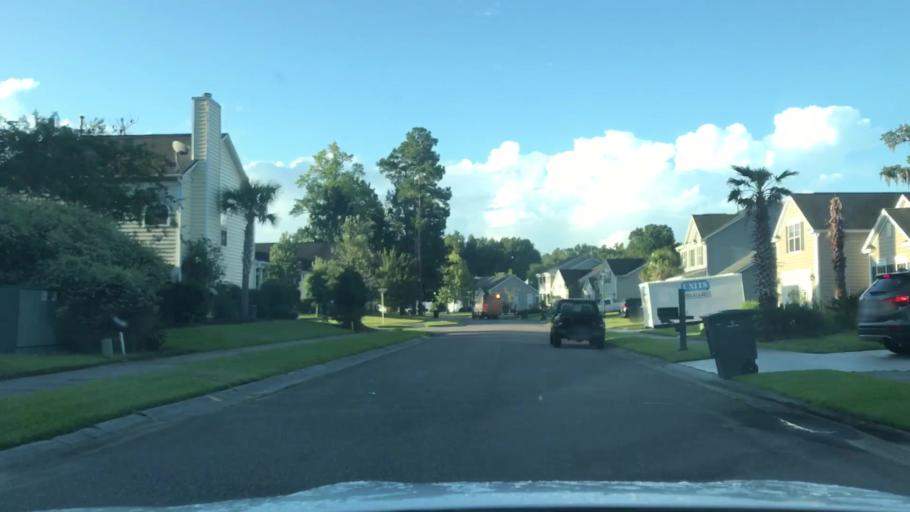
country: US
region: South Carolina
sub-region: Charleston County
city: Shell Point
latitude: 32.8363
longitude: -80.1018
